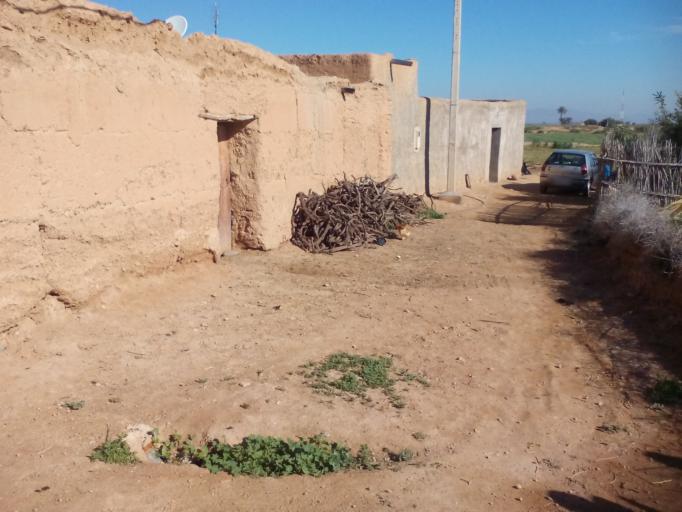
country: MA
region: Marrakech-Tensift-Al Haouz
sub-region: Marrakech
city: Marrakesh
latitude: 31.6372
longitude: -8.3004
